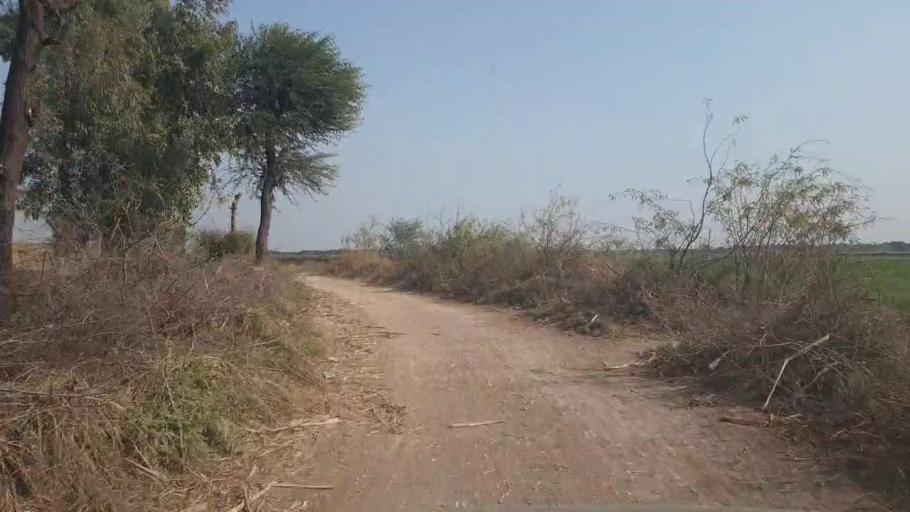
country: PK
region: Sindh
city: Tando Allahyar
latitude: 25.4497
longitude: 68.7935
